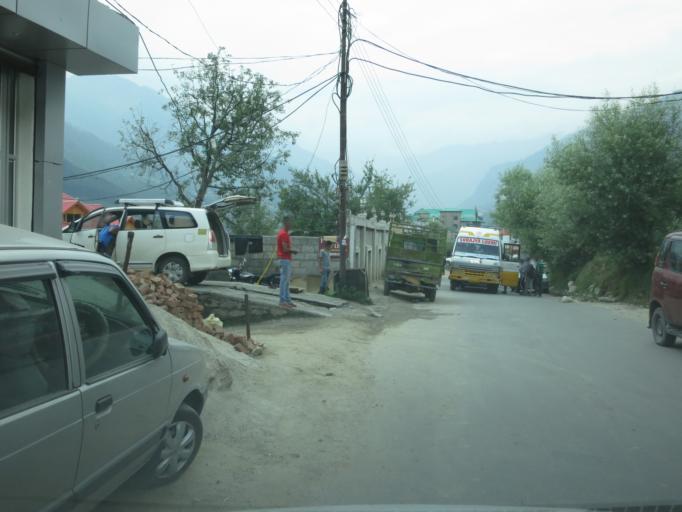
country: IN
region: Himachal Pradesh
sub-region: Kulu
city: Manali
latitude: 32.2216
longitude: 77.1964
